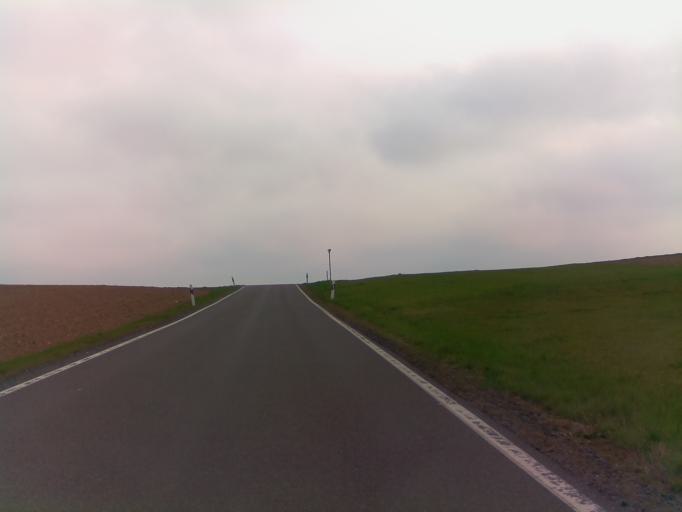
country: DE
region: Rheinland-Pfalz
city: Leisel
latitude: 49.7235
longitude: 7.2152
